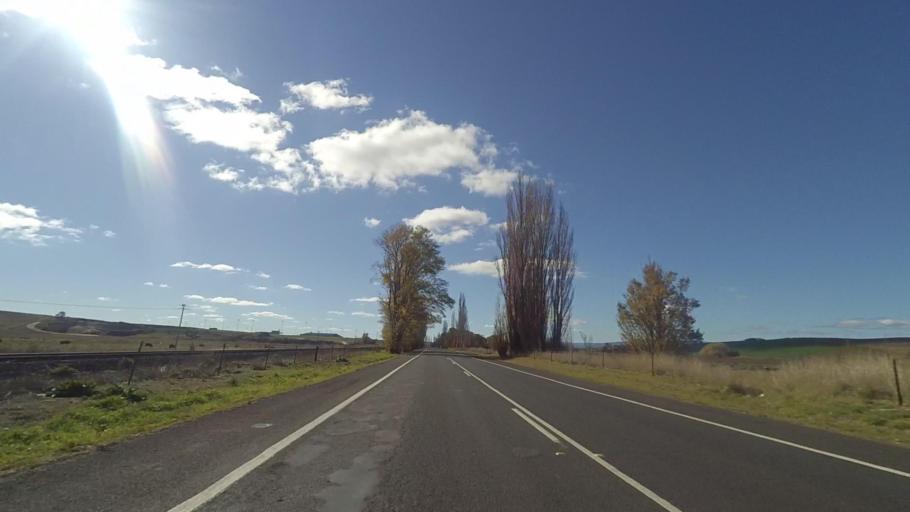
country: AU
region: New South Wales
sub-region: Bathurst Regional
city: Perthville
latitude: -33.4585
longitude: 149.5738
